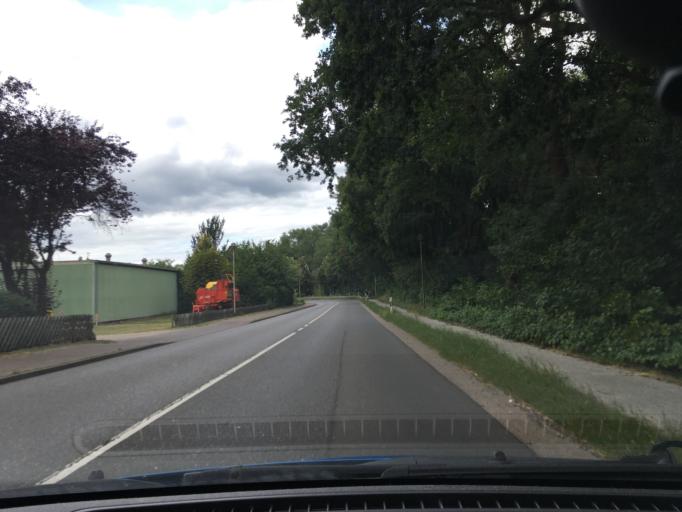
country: DE
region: Lower Saxony
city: Neu Wulmstorf
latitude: 53.4470
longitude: 9.7571
